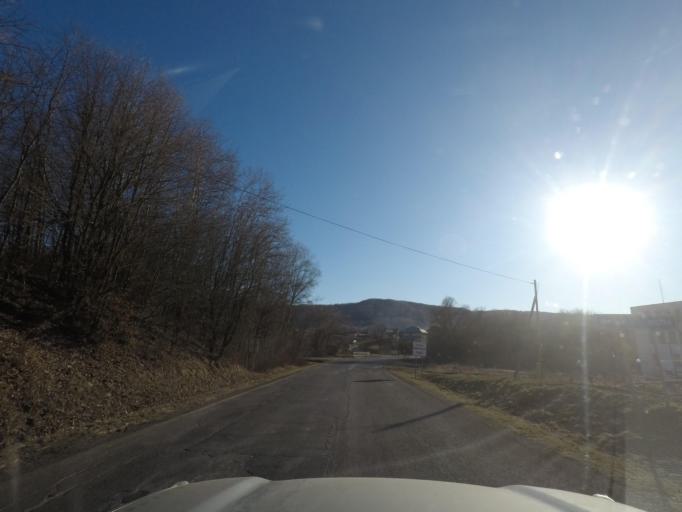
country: SK
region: Presovsky
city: Medzilaborce
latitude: 49.2585
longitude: 21.7920
